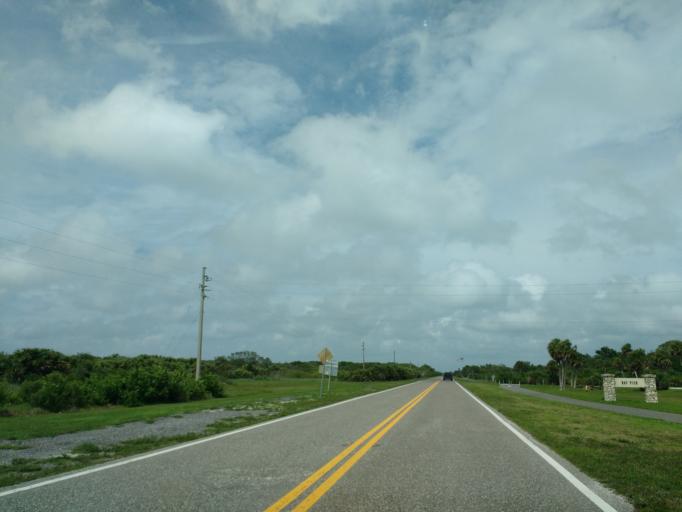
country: US
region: Florida
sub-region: Pinellas County
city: Tierra Verde
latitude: 27.6174
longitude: -82.7276
